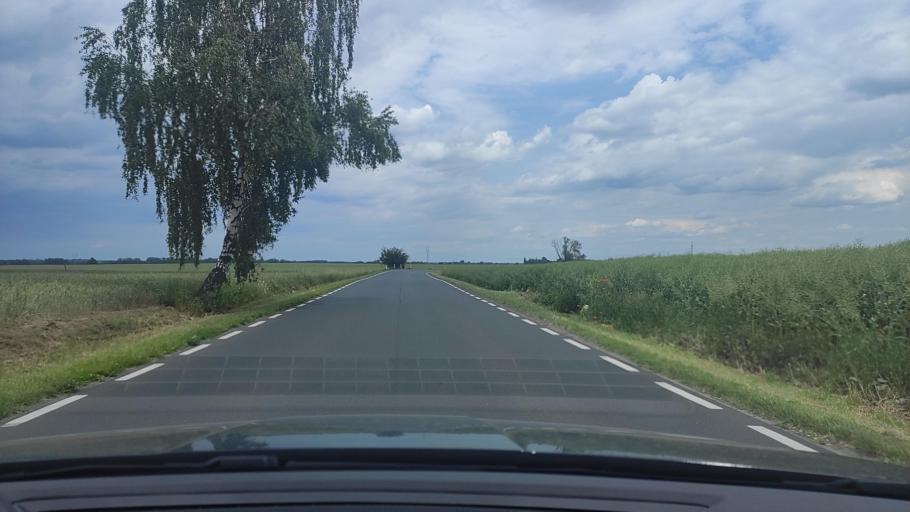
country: PL
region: Greater Poland Voivodeship
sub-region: Powiat poznanski
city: Swarzedz
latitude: 52.4295
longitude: 17.1586
